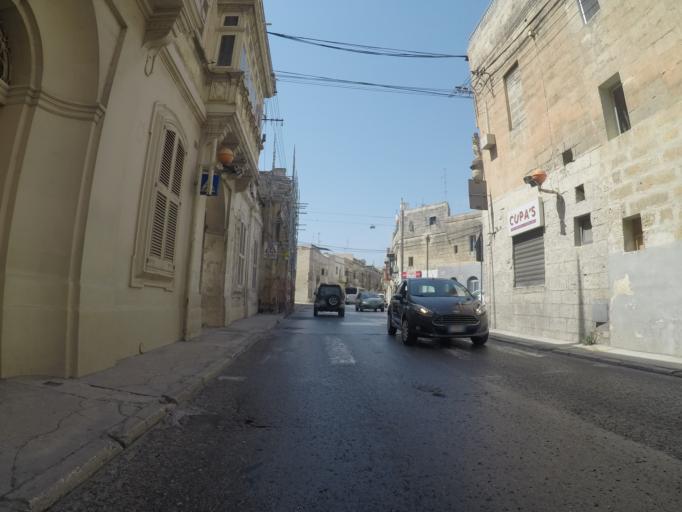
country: MT
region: Ir-Rabat
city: Rabat
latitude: 35.8785
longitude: 14.4006
